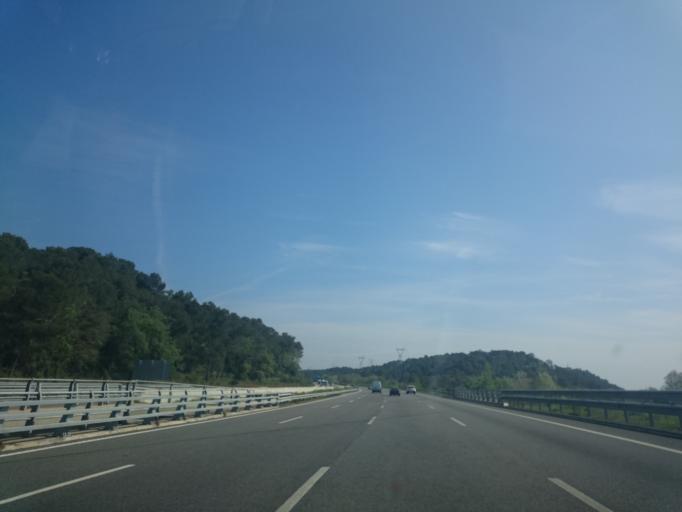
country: ES
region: Catalonia
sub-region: Provincia de Girona
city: Celra
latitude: 42.0555
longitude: 2.8811
